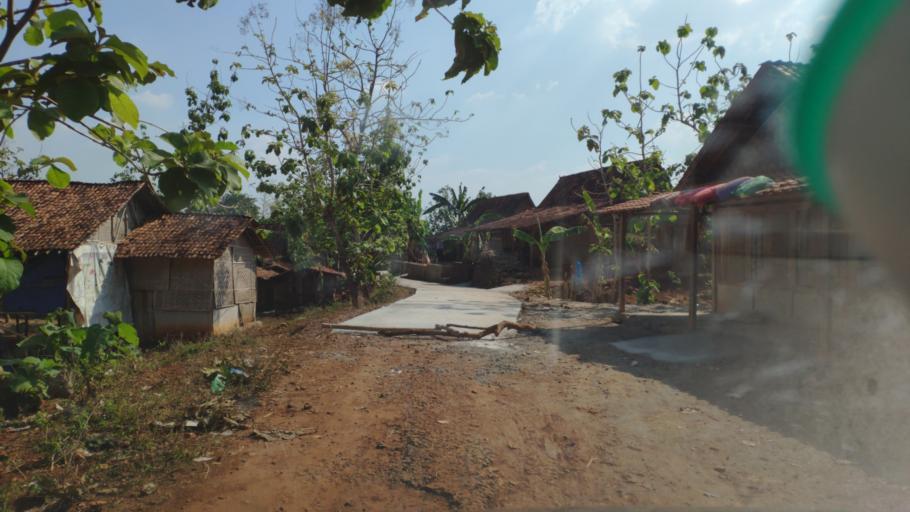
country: ID
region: Central Java
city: Ngapus
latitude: -6.9380
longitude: 111.2113
